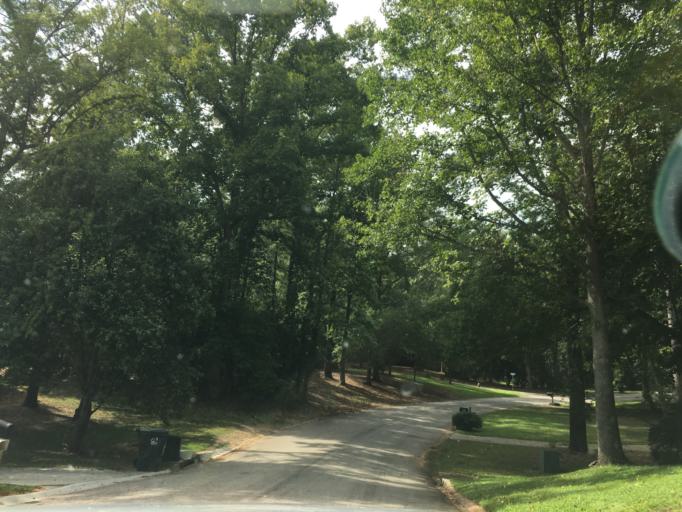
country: US
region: South Carolina
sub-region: Lexington County
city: Irmo
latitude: 34.0628
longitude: -81.1866
